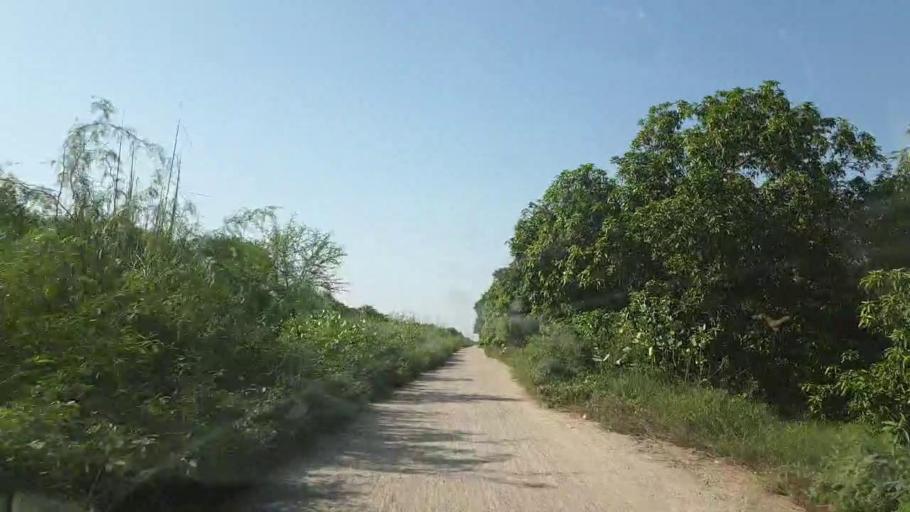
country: PK
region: Sindh
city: Tando Jam
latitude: 25.3298
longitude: 68.5908
